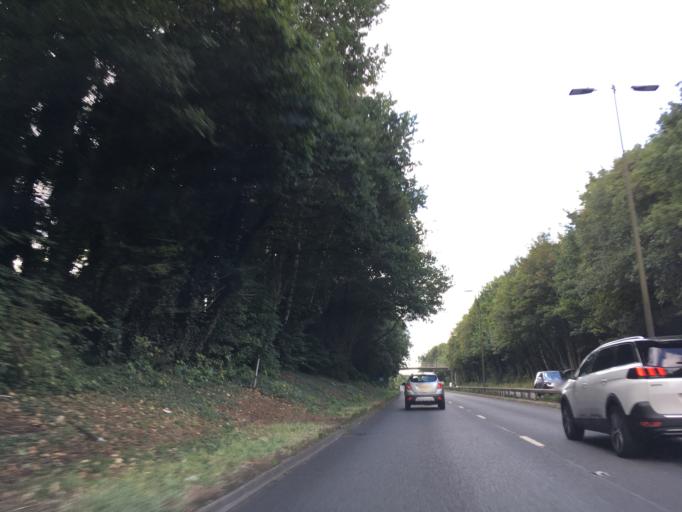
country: GB
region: England
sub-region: West Berkshire
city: Greenham
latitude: 51.3895
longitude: -1.3199
